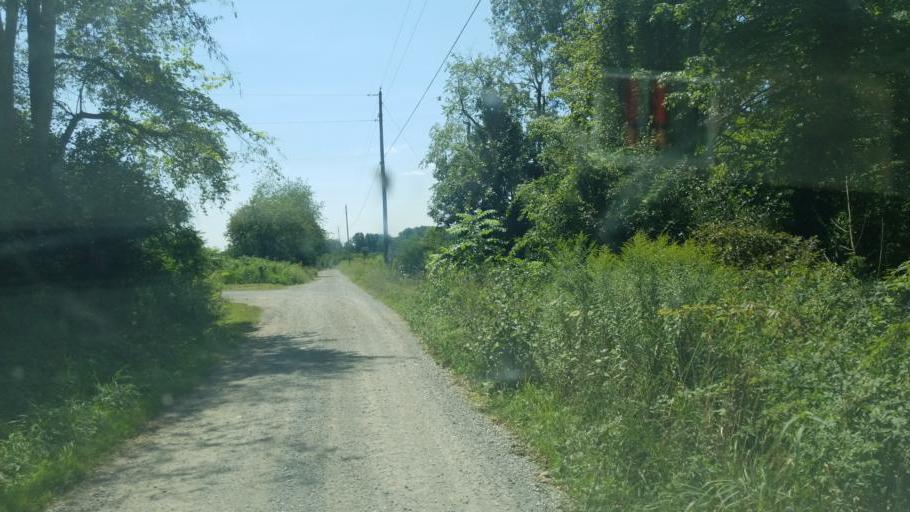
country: US
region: Pennsylvania
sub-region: Clarion County
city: Knox
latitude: 41.1971
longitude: -79.6479
